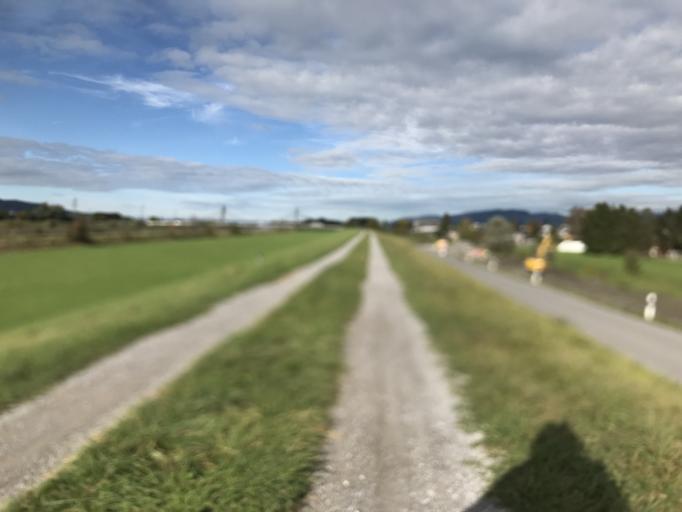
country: CH
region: Saint Gallen
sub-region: Wahlkreis Rheintal
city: Diepoldsau
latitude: 47.3836
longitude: 9.6440
